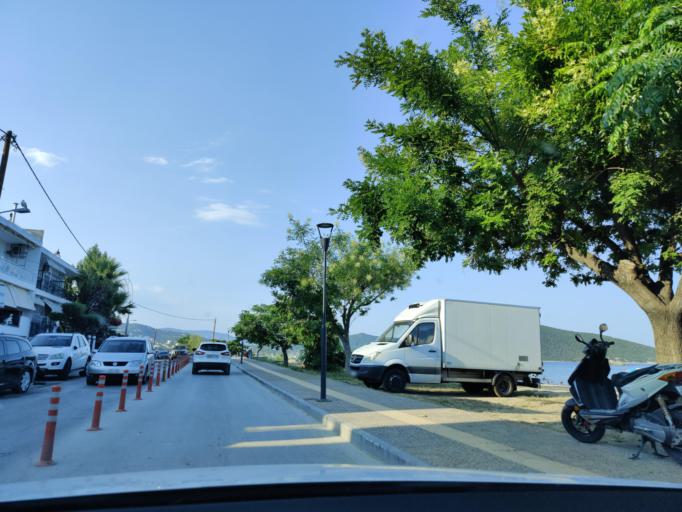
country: GR
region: East Macedonia and Thrace
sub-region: Nomos Kavalas
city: Nea Peramos
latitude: 40.8347
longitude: 24.3051
